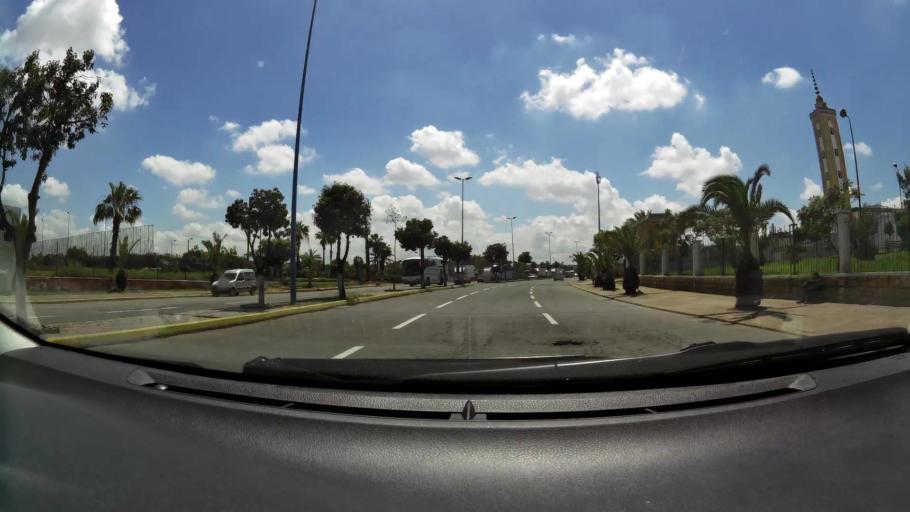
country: MA
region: Grand Casablanca
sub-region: Casablanca
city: Casablanca
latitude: 33.5690
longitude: -7.5780
